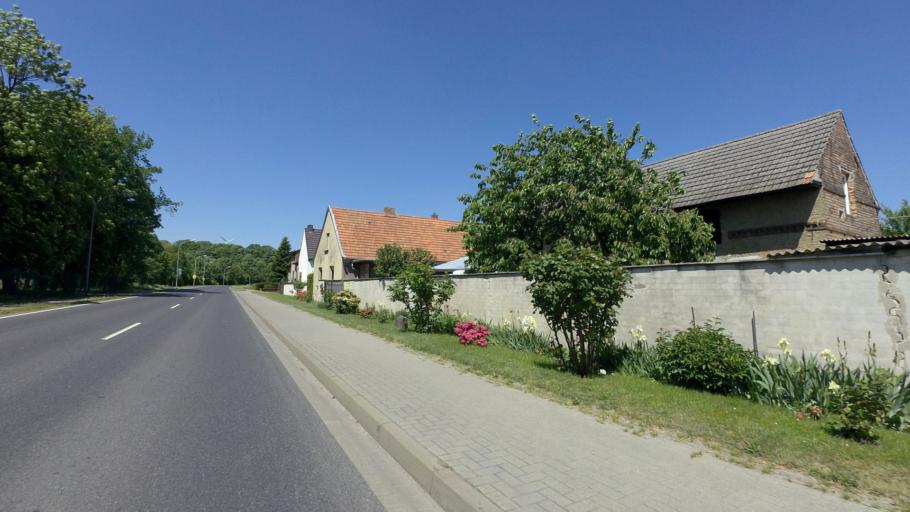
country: DE
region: Brandenburg
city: Drehnow
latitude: 51.8707
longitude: 14.3801
